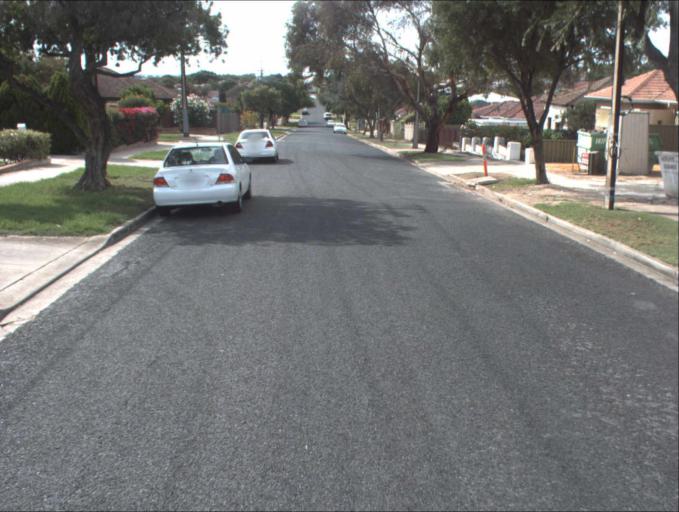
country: AU
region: South Australia
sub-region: Port Adelaide Enfield
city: Blair Athol
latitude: -34.8695
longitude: 138.5978
